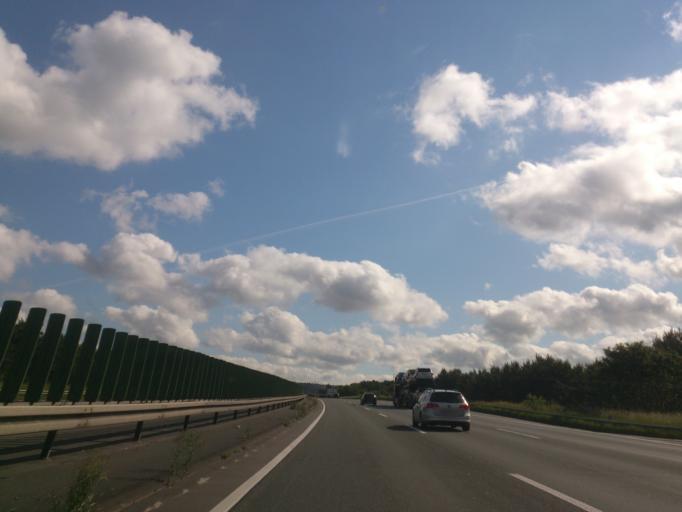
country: DE
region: North Rhine-Westphalia
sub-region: Regierungsbezirk Detmold
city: Verl
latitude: 51.9522
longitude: 8.5660
